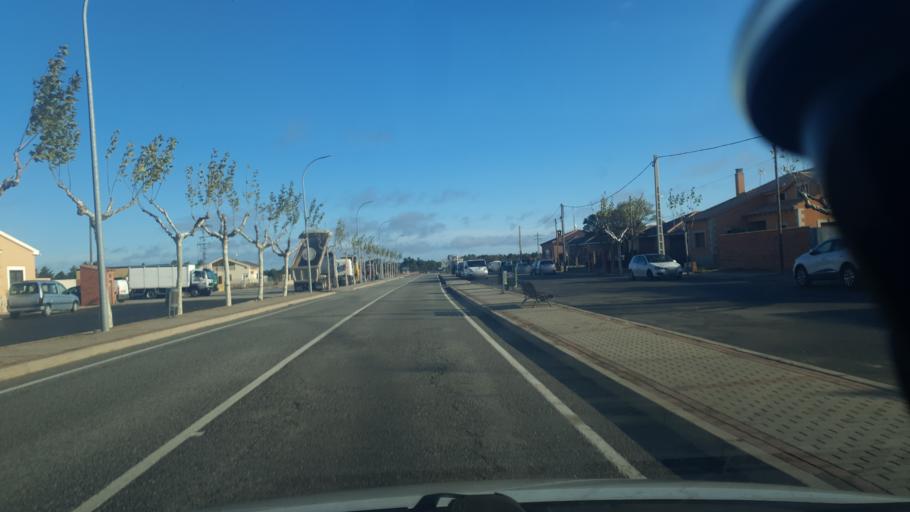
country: ES
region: Castille and Leon
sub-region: Provincia de Avila
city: Tinosillos
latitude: 40.9385
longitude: -4.7251
